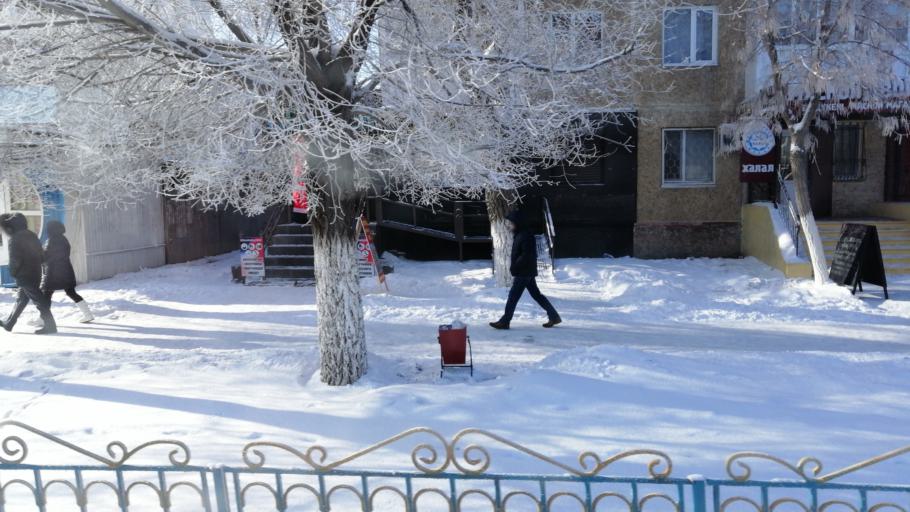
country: KZ
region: Aqtoebe
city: Aqtobe
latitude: 50.3035
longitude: 57.1522
